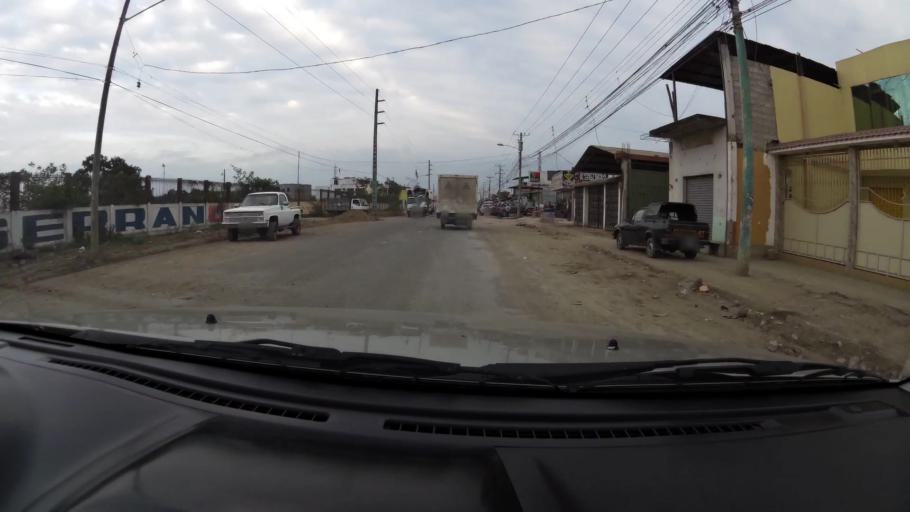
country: EC
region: El Oro
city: Machala
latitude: -3.2698
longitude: -79.9362
